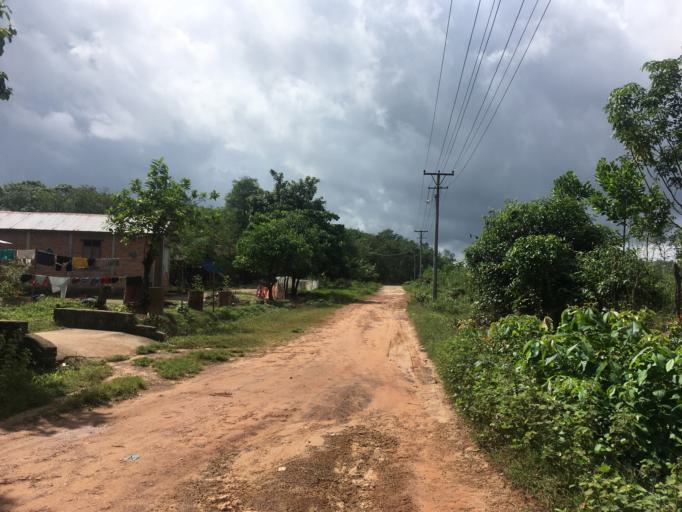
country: MM
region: Mon
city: Mawlamyine
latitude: 16.4642
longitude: 97.6906
